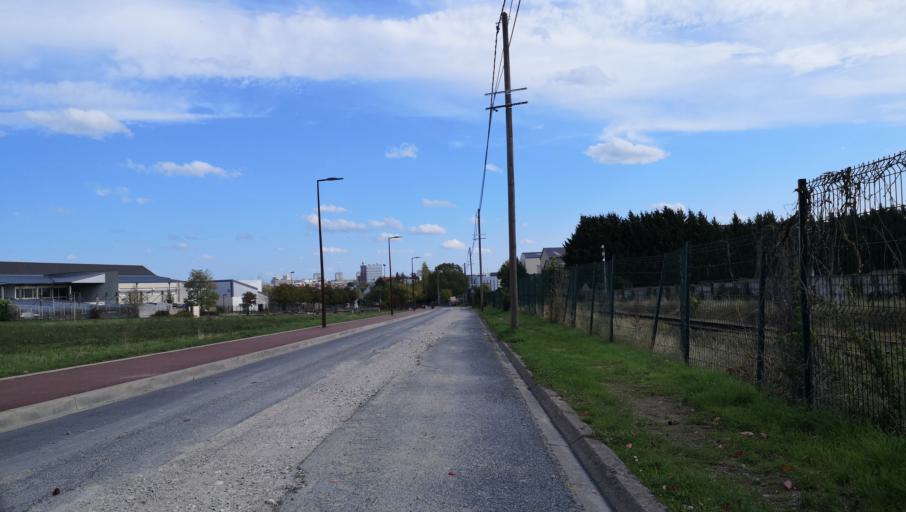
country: FR
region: Centre
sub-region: Departement du Loiret
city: Saint-Jean-de-la-Ruelle
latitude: 47.9178
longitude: 1.8759
